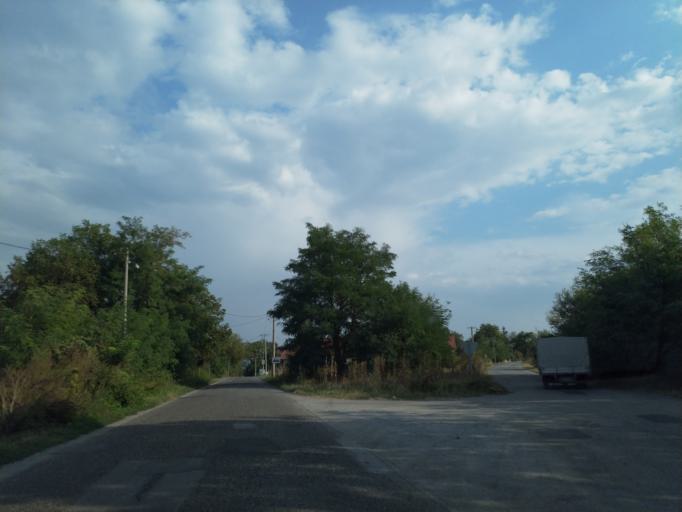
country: RS
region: Central Serbia
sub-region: Pomoravski Okrug
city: Paracin
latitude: 43.8439
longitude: 21.4705
